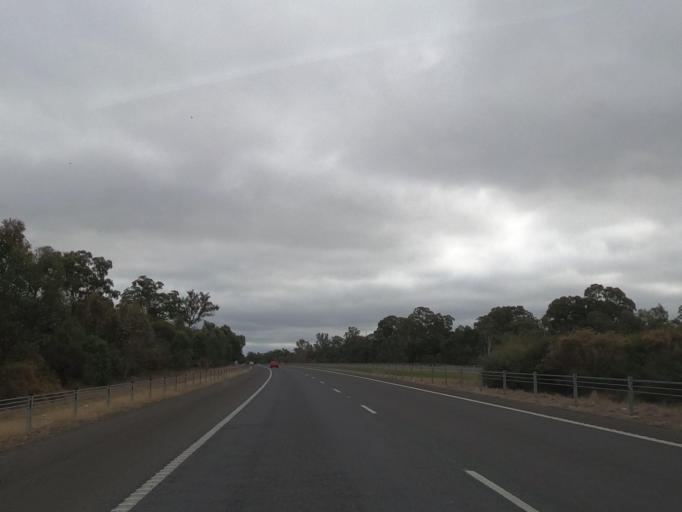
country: AU
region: Victoria
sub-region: Mount Alexander
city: Castlemaine
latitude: -37.0990
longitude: 144.3643
